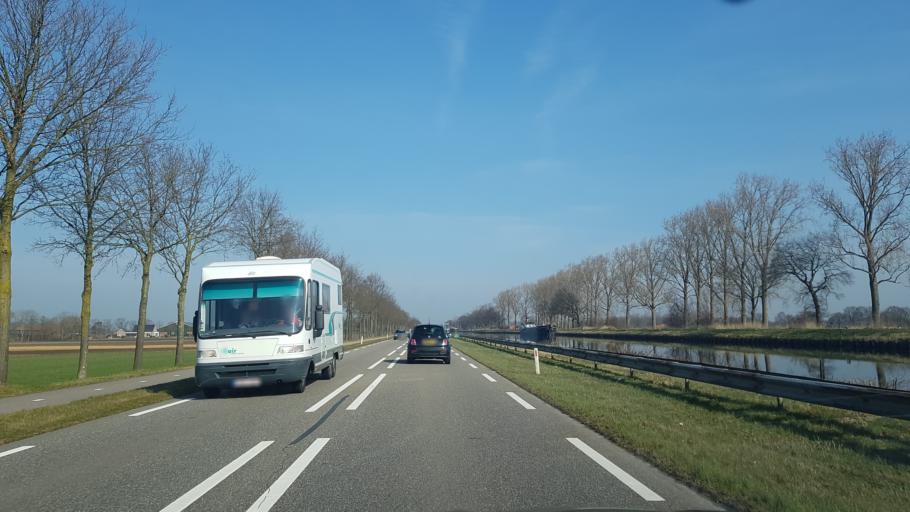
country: NL
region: Limburg
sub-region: Gemeente Nederweert
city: Nederweert
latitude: 51.3219
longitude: 5.7478
